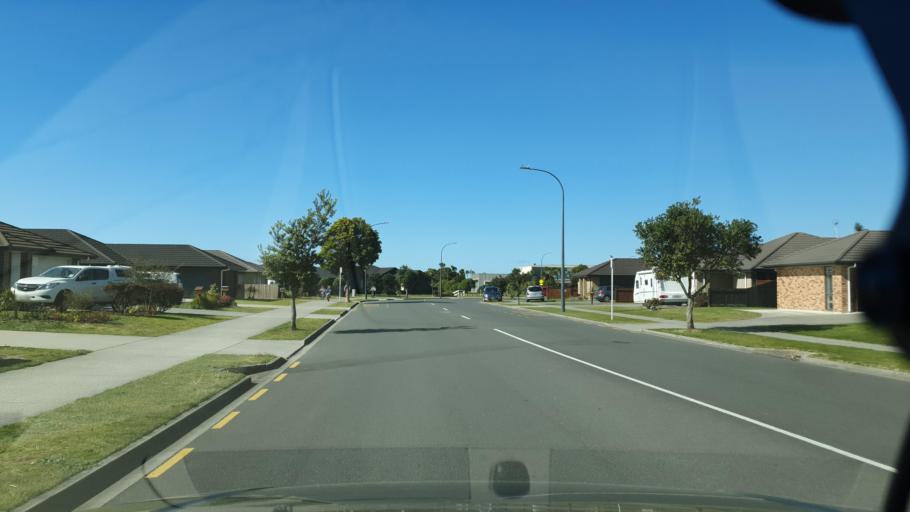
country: NZ
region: Bay of Plenty
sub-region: Tauranga City
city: Tauranga
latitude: -37.7102
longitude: 176.2993
